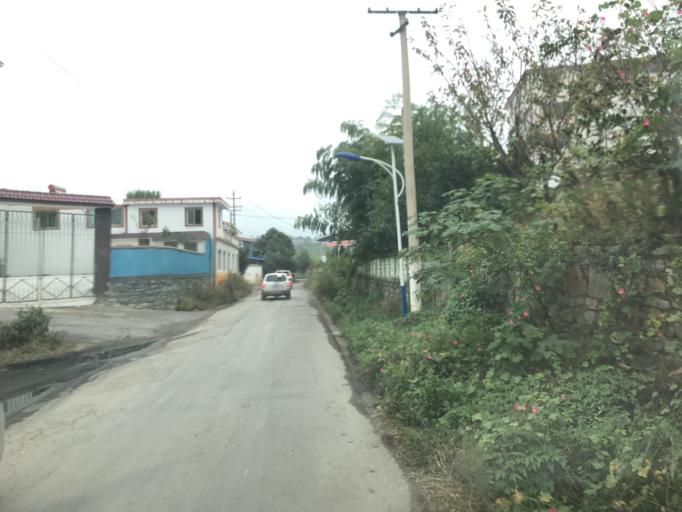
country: CN
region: Guizhou Sheng
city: Guiyang
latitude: 26.7062
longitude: 106.8786
